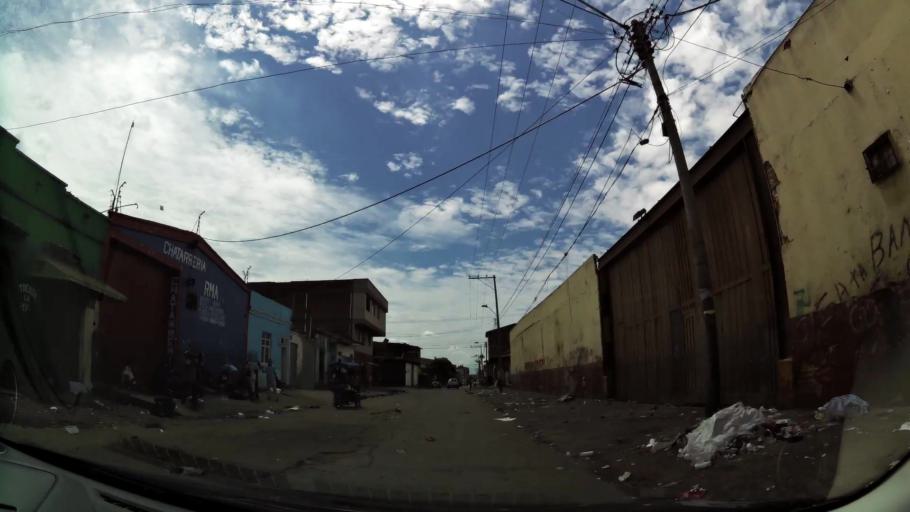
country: CO
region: Valle del Cauca
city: Cali
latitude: 3.4465
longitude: -76.5251
